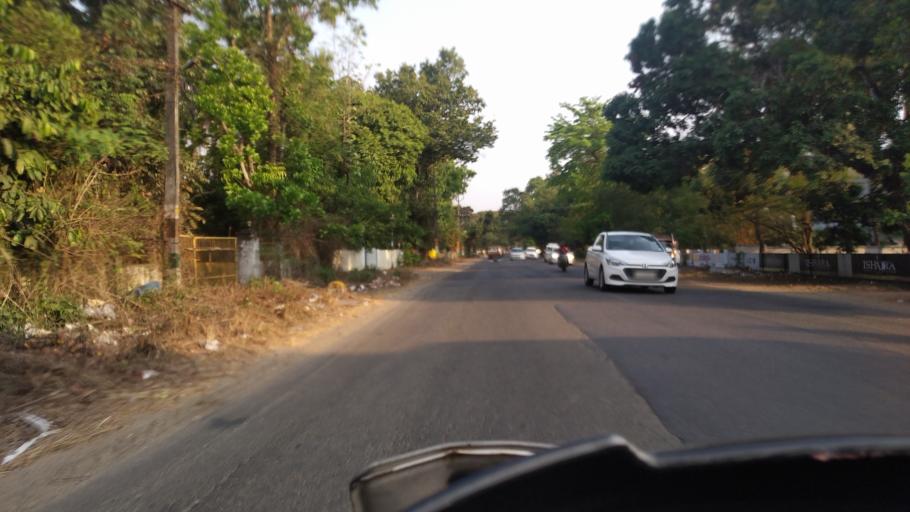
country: IN
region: Kerala
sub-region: Thrissur District
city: Thanniyam
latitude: 10.4340
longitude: 76.0982
